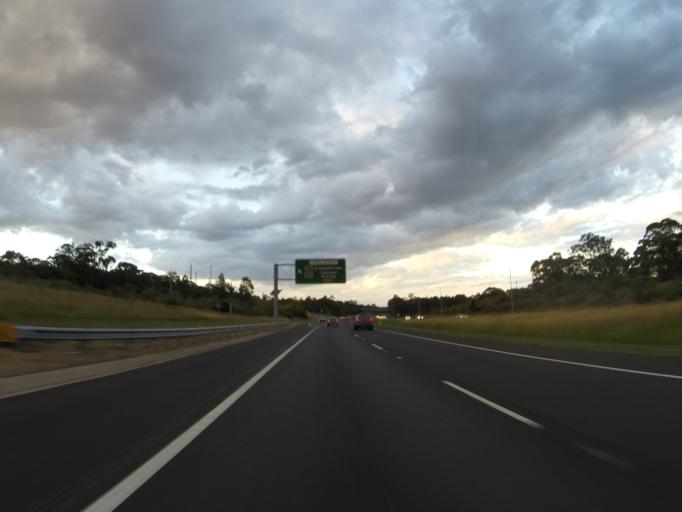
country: AU
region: New South Wales
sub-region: Campbelltown Municipality
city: Glen Alpine
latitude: -34.0657
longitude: 150.7813
